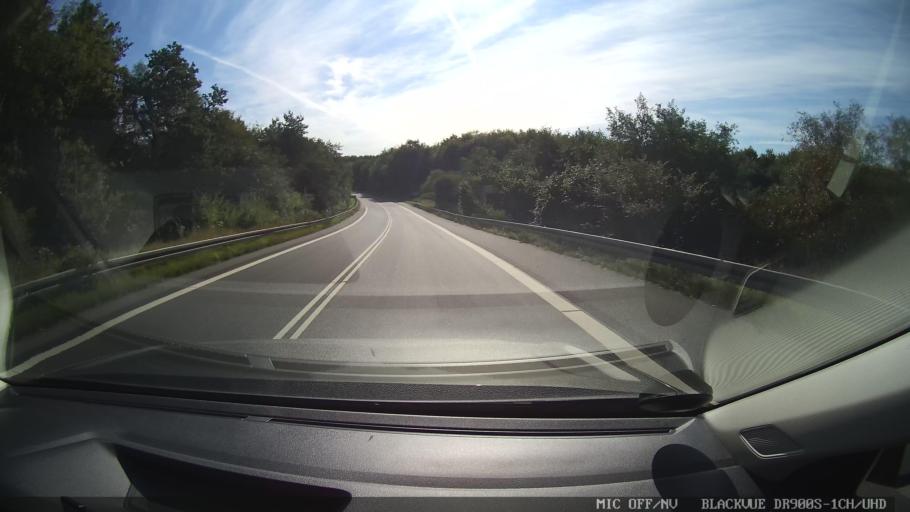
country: DK
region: North Denmark
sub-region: Mariagerfjord Kommune
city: Arden
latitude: 56.7750
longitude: 9.7763
